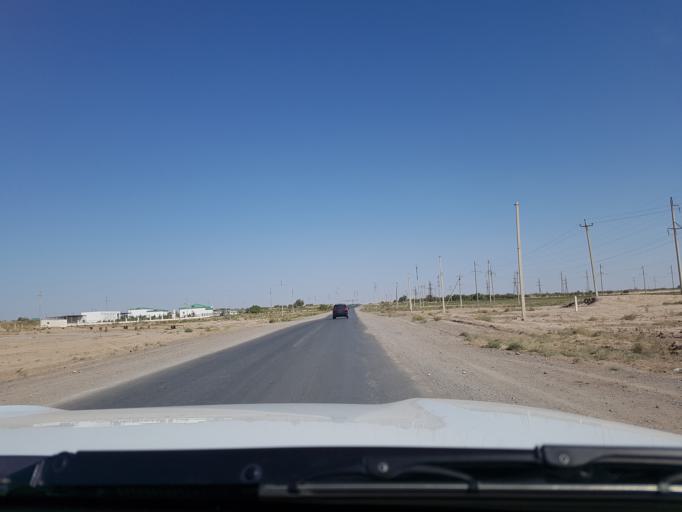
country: IR
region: Razavi Khorasan
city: Sarakhs
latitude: 36.5239
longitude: 61.2307
